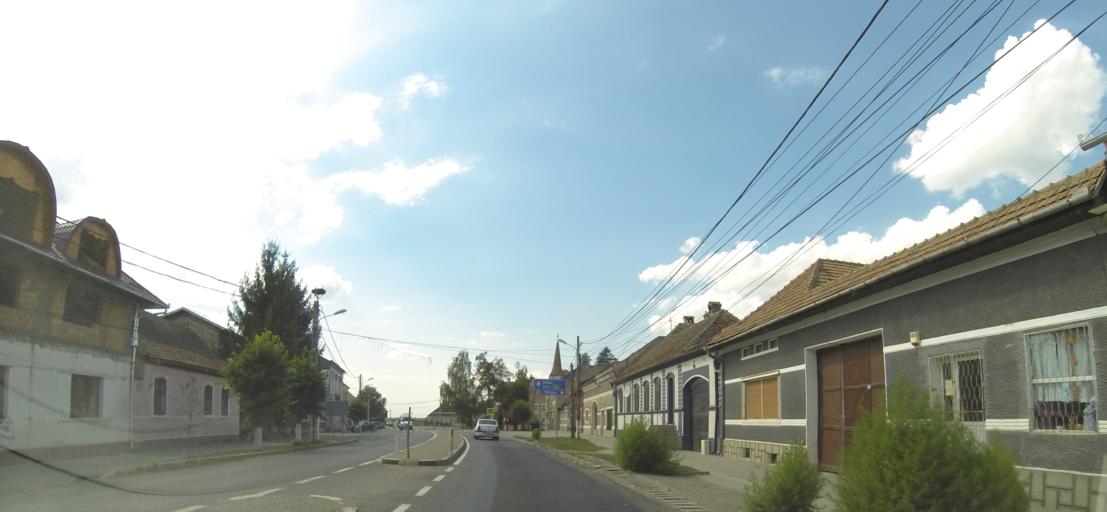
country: RO
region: Brasov
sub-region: Comuna Sercaia
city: Sercaia
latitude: 45.8308
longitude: 25.1397
